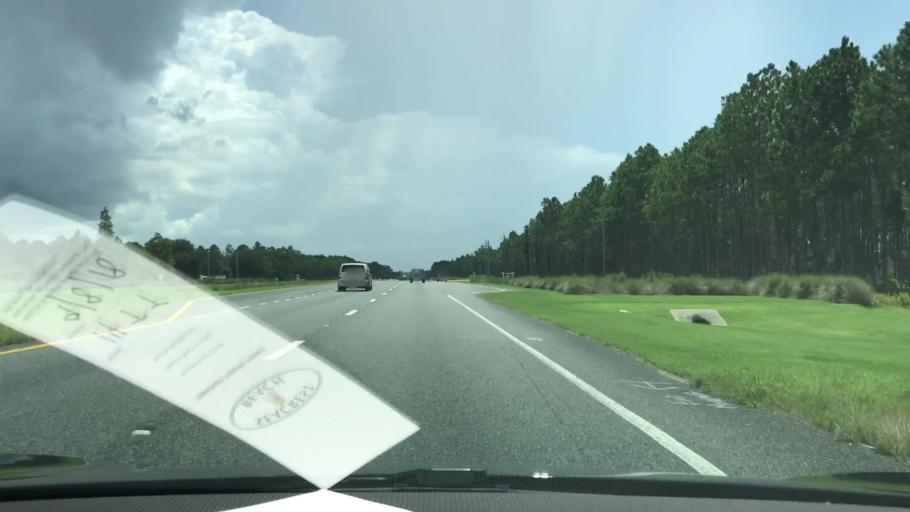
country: US
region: Florida
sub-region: Bay County
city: Laguna Beach
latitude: 30.2975
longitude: -86.0263
